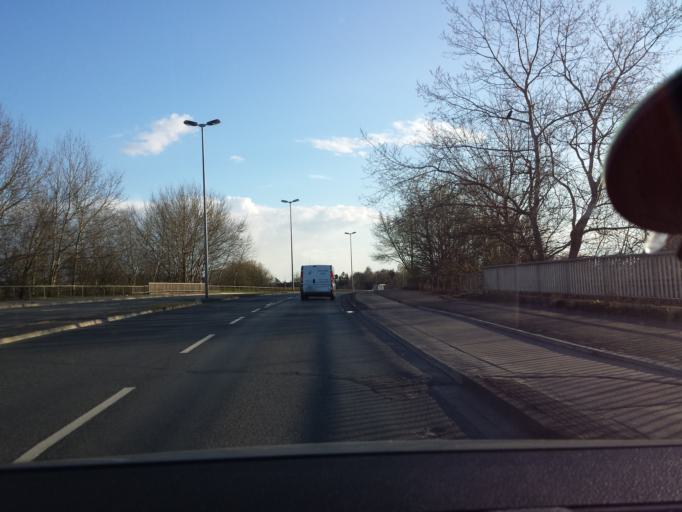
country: DE
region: Lower Saxony
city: Braunschweig
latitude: 52.3119
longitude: 10.4958
